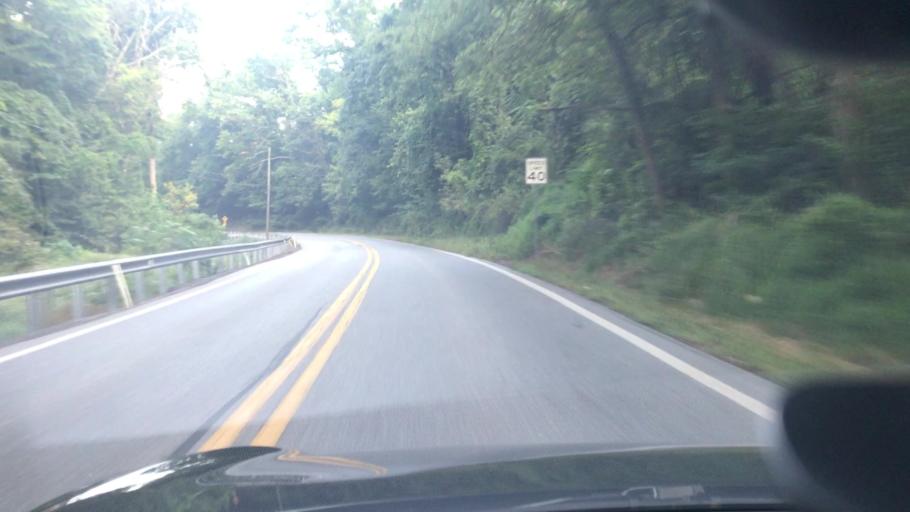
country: US
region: Pennsylvania
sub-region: Cumberland County
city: Lower Allen
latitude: 40.1625
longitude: -76.8915
